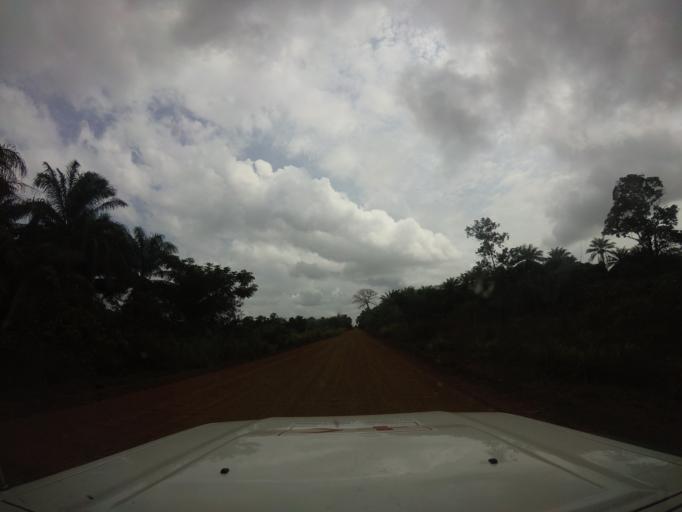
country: LR
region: Grand Cape Mount
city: Robertsport
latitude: 6.7381
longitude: -11.3396
